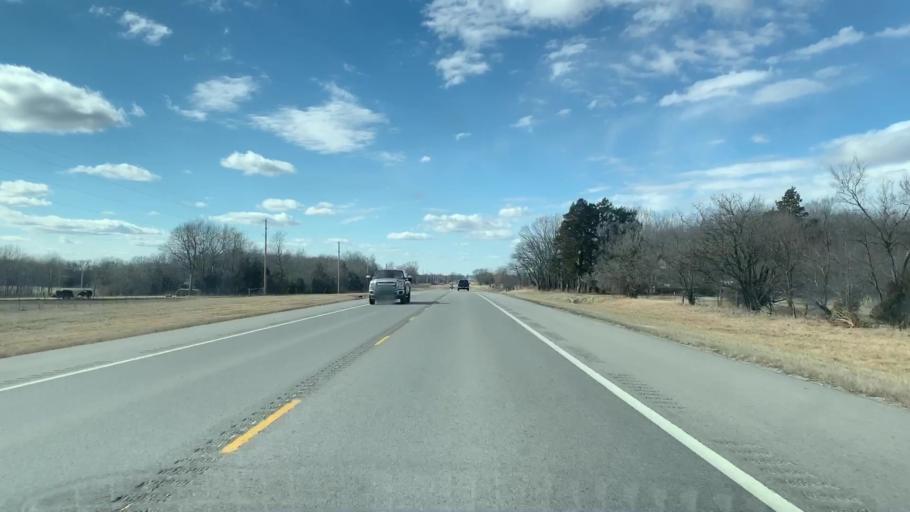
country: US
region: Kansas
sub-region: Labette County
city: Oswego
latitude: 37.3399
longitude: -95.0595
